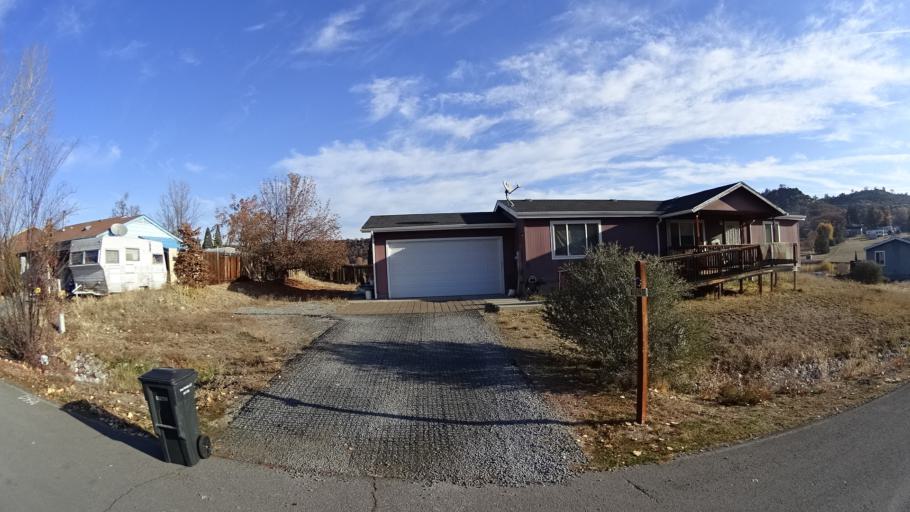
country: US
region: California
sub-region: Siskiyou County
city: Yreka
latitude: 41.7076
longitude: -122.6206
